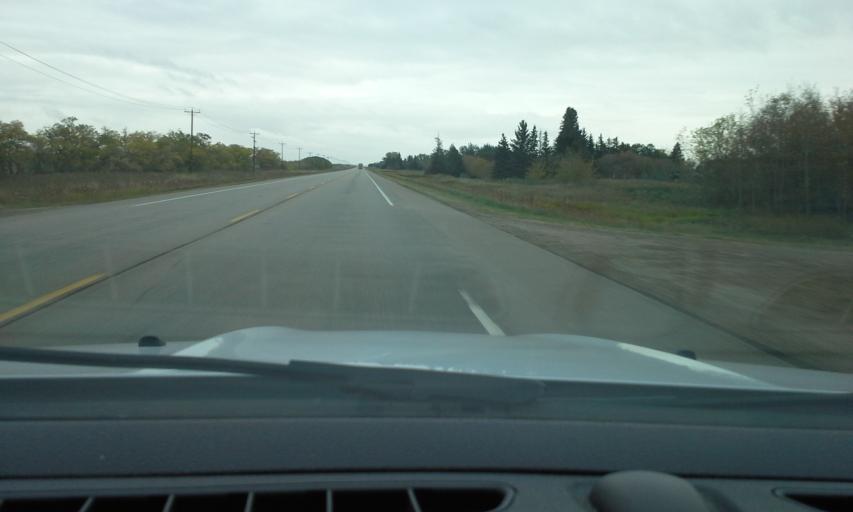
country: CA
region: Saskatchewan
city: Lloydminster
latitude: 53.2780
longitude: -109.8576
